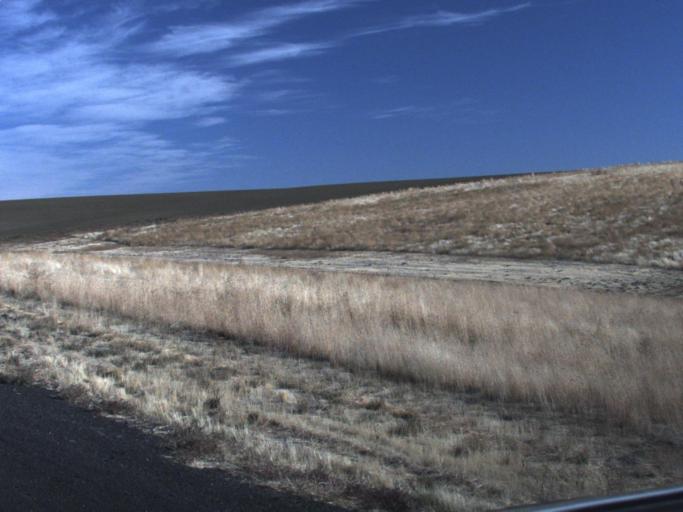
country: US
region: Washington
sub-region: Adams County
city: Ritzville
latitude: 47.1453
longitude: -118.6869
